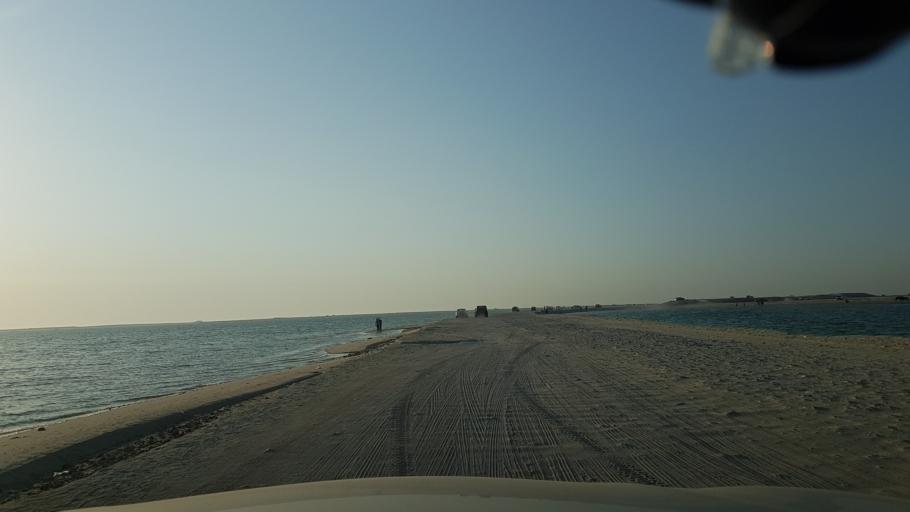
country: BH
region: Manama
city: Jidd Hafs
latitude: 26.2383
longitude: 50.5044
